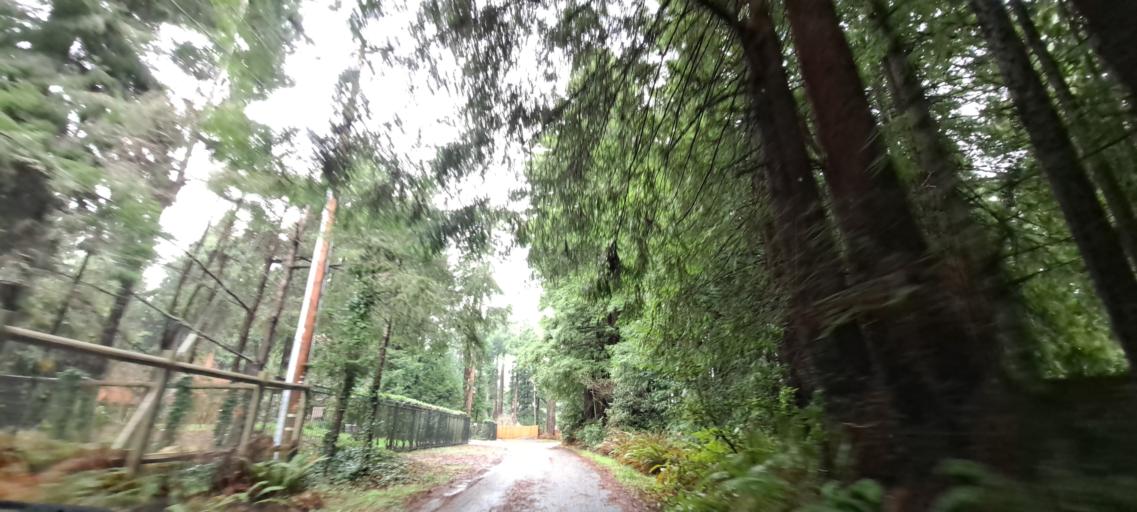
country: US
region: California
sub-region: Humboldt County
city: Fortuna
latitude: 40.6057
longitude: -124.1396
